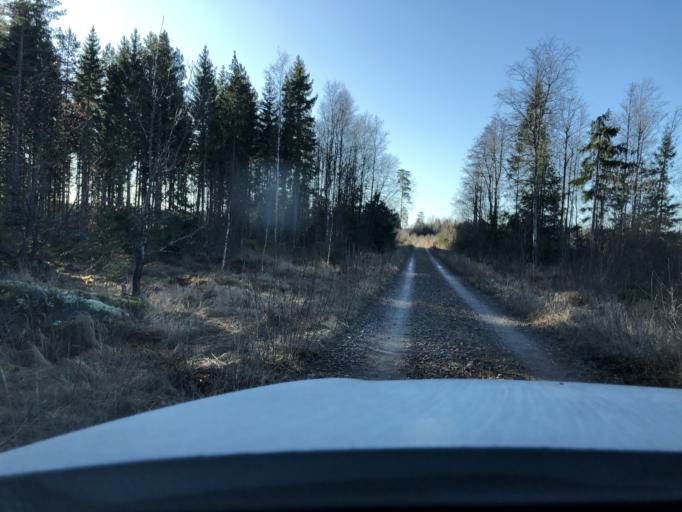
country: SE
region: Gaevleborg
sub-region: Gavle Kommun
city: Hedesunda
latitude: 60.3014
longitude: 16.8920
